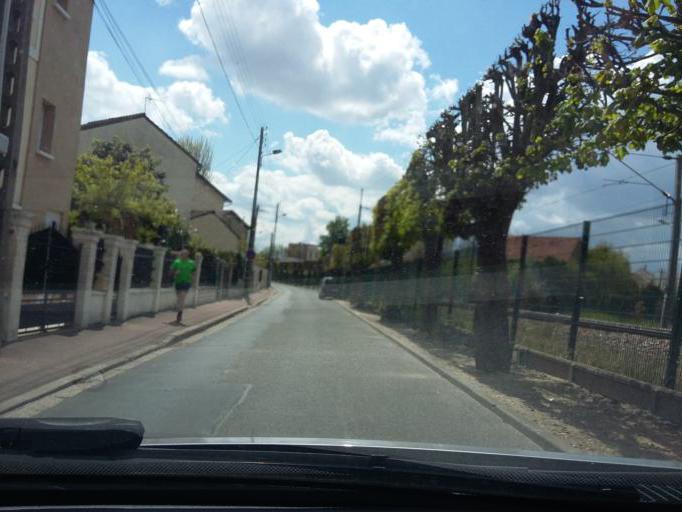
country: FR
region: Ile-de-France
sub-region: Departement du Val-d'Oise
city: Ermont
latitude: 48.9845
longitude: 2.2651
